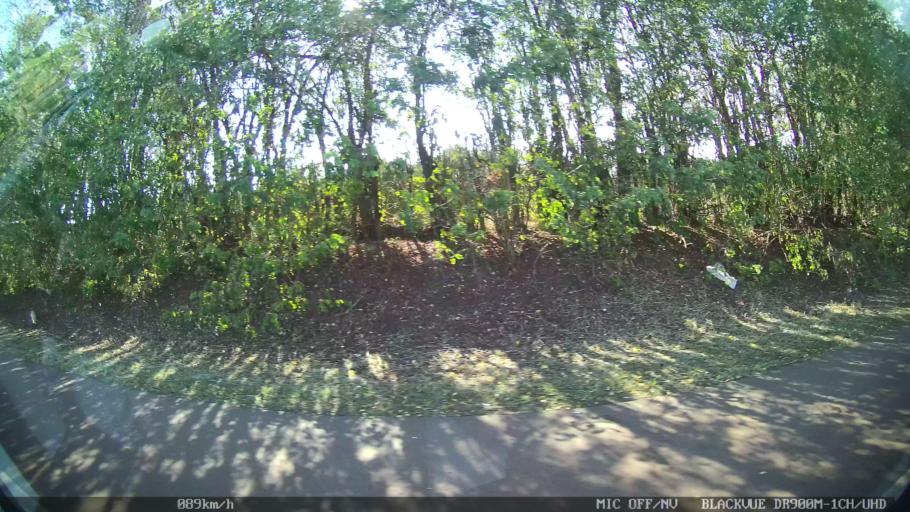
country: BR
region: Sao Paulo
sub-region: Iracemapolis
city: Iracemapolis
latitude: -22.6683
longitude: -47.5390
